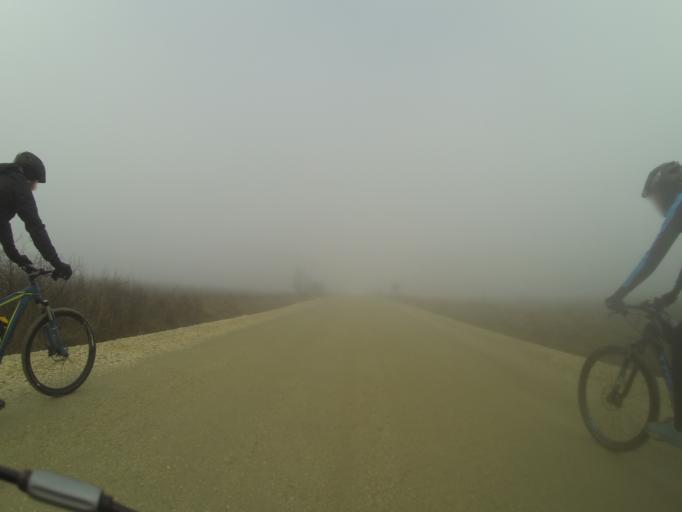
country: RO
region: Mehedinti
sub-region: Comuna Baclesu
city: Baclesu
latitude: 44.4441
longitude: 23.1285
